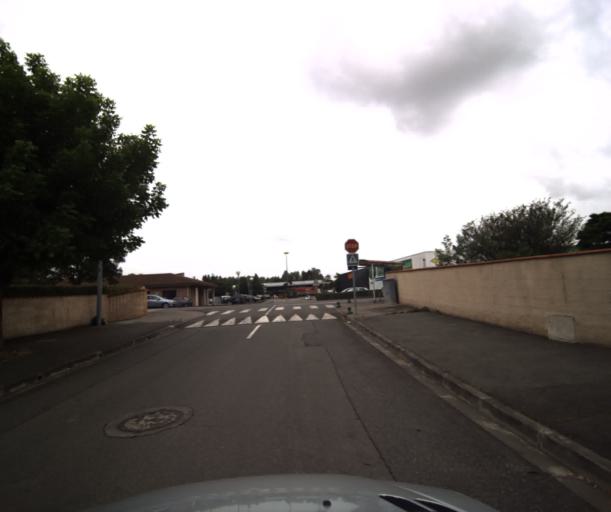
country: FR
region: Midi-Pyrenees
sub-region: Departement de la Haute-Garonne
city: Pinsaguel
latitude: 43.5008
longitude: 1.3935
